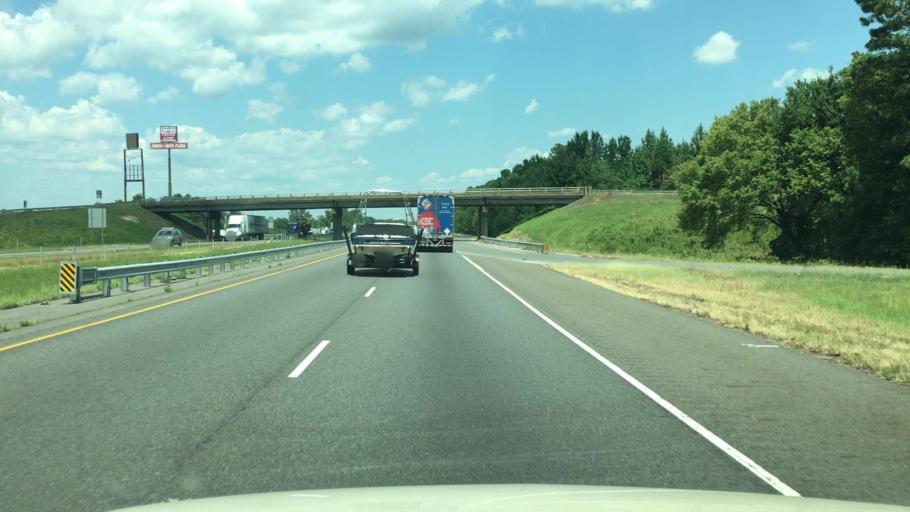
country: US
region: Arkansas
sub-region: Clark County
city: Gurdon
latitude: 33.9959
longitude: -93.1847
